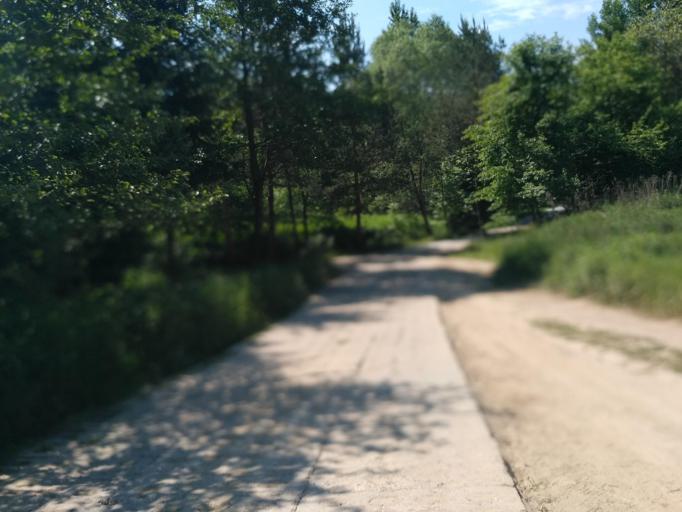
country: PL
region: Subcarpathian Voivodeship
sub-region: Powiat brzozowski
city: Golcowa
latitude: 49.8168
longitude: 22.0468
